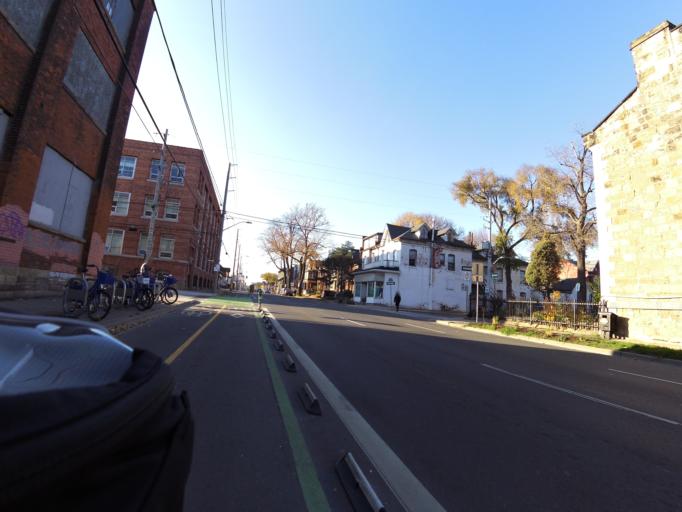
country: CA
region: Ontario
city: Hamilton
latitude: 43.2594
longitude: -79.8618
